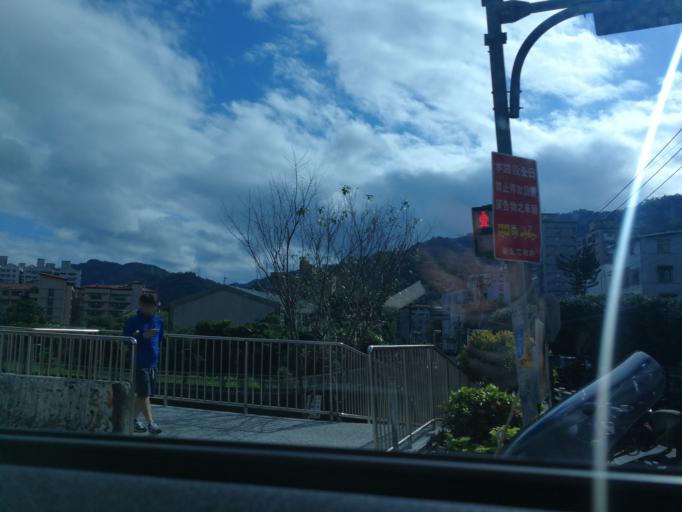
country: TW
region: Taipei
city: Taipei
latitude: 24.9518
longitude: 121.5501
